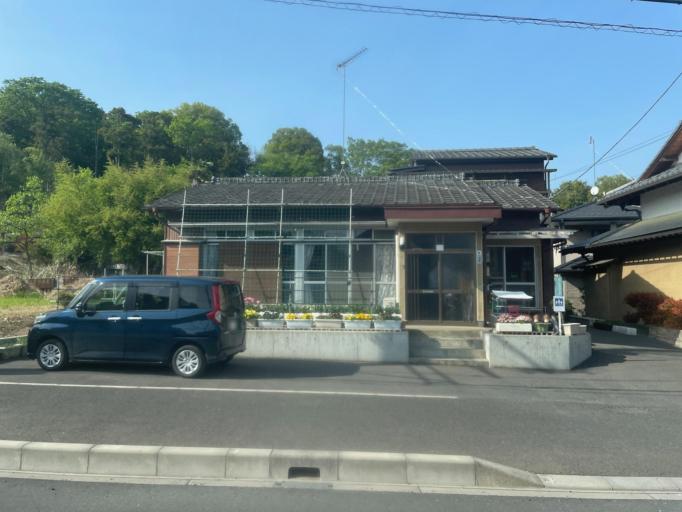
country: JP
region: Tochigi
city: Ashikaga
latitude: 36.3161
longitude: 139.5032
